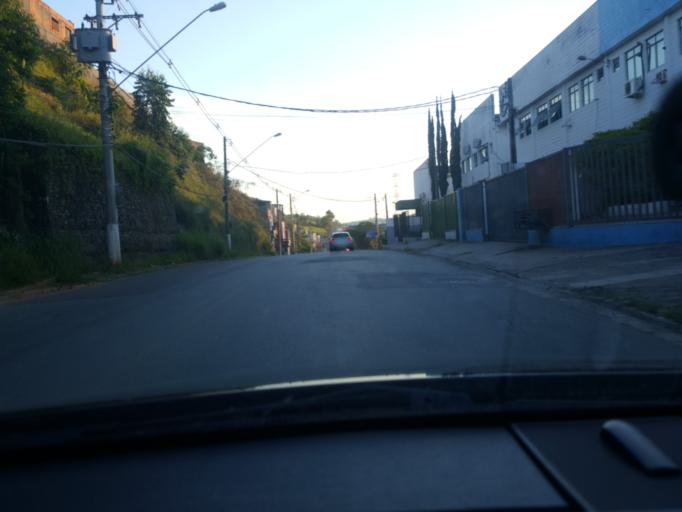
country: BR
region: Sao Paulo
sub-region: Cajamar
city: Cajamar
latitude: -23.3856
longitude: -46.8627
